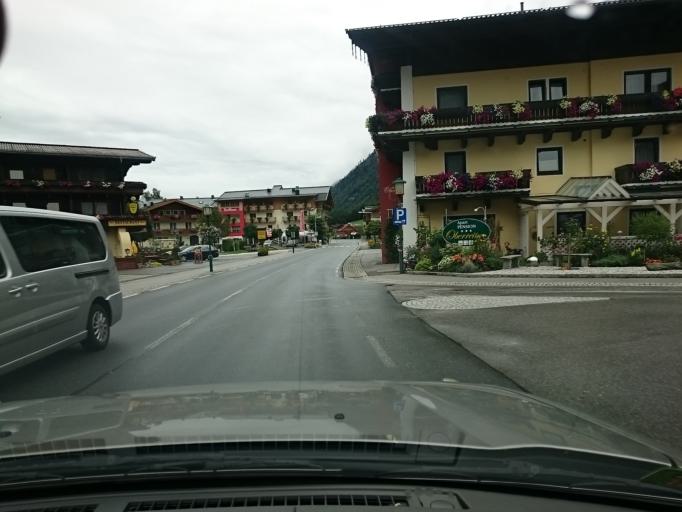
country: AT
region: Salzburg
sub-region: Politischer Bezirk Zell am See
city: Bruck an der Grossglocknerstrasse
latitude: 47.2263
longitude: 12.8264
